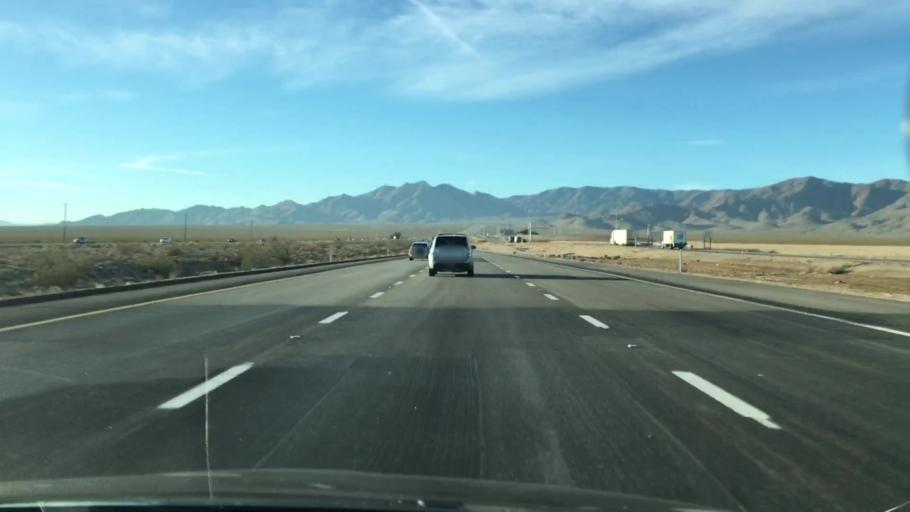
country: US
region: Nevada
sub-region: Clark County
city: Sandy Valley
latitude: 35.5129
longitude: -115.4326
